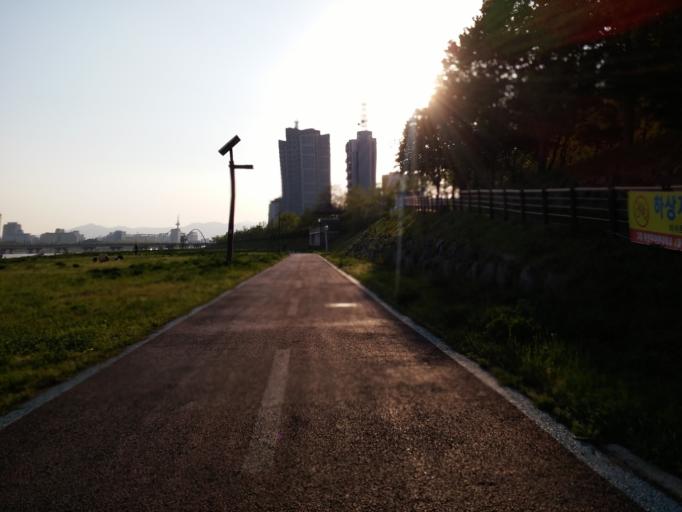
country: KR
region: Daejeon
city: Songgang-dong
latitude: 36.3758
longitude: 127.4005
